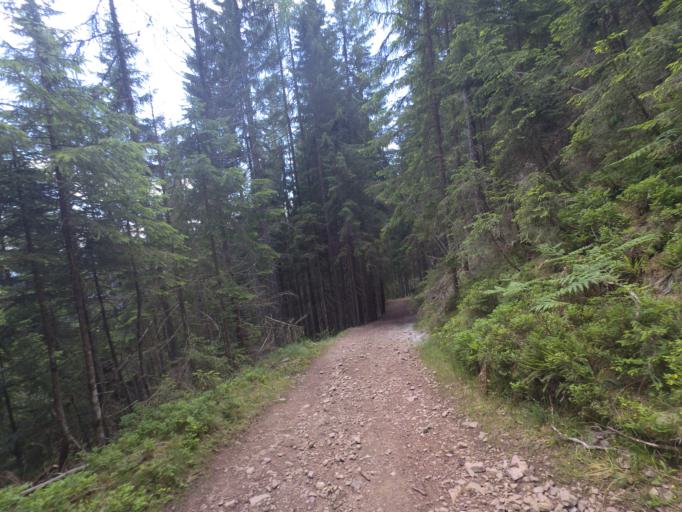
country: AT
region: Salzburg
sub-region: Politischer Bezirk Zell am See
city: Leogang
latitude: 47.4596
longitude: 12.7709
